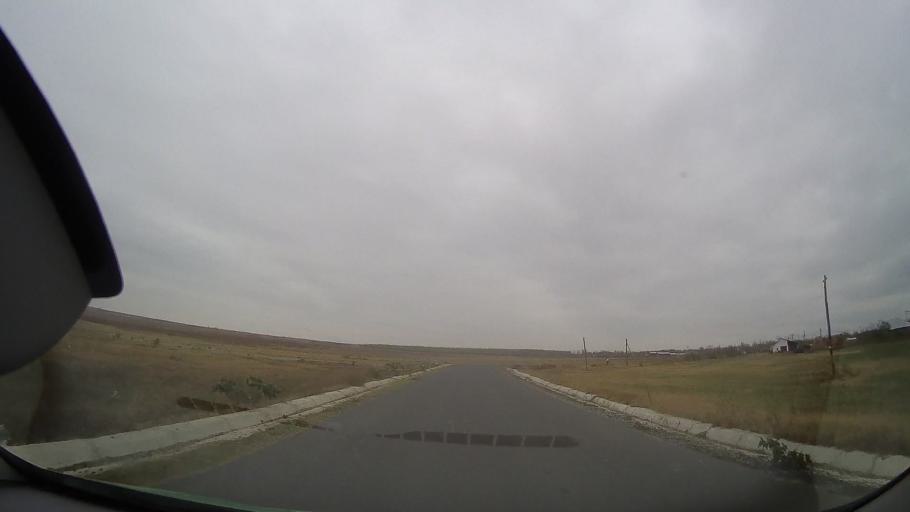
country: RO
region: Braila
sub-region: Comuna Ciocile
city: Ciocile
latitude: 44.7994
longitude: 27.2729
